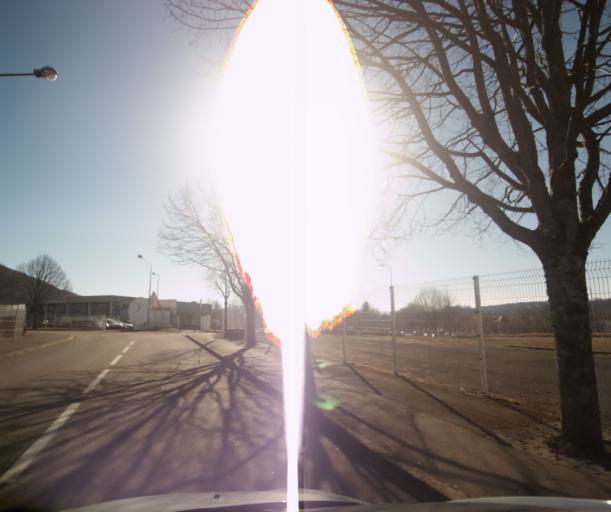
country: FR
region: Franche-Comte
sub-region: Departement du Doubs
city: Avanne-Aveney
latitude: 47.2134
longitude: 5.9680
